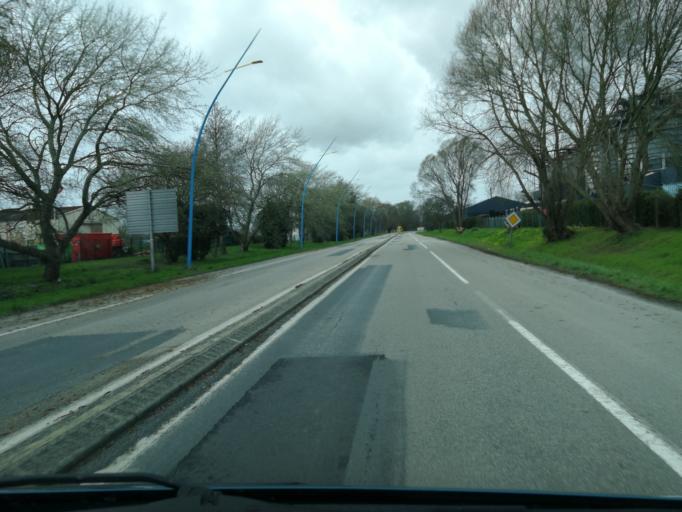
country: FR
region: Haute-Normandie
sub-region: Departement de l'Eure
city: Quillebeuf-sur-Seine
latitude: 49.4746
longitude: 0.5351
